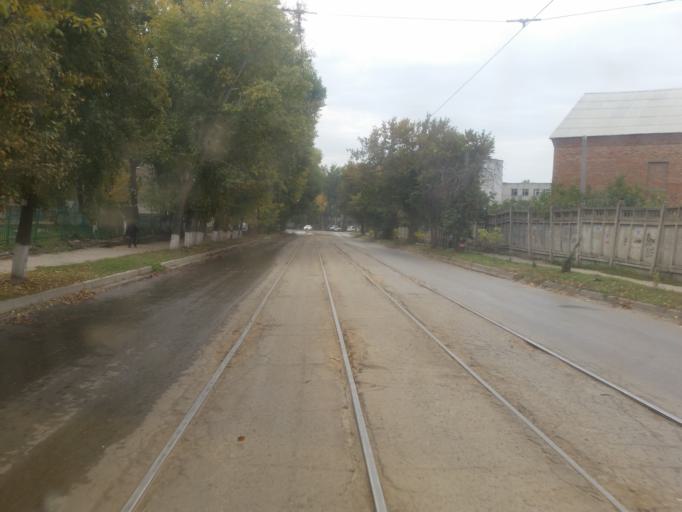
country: RU
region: Ulyanovsk
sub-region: Ulyanovskiy Rayon
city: Ulyanovsk
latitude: 54.3264
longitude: 48.3859
